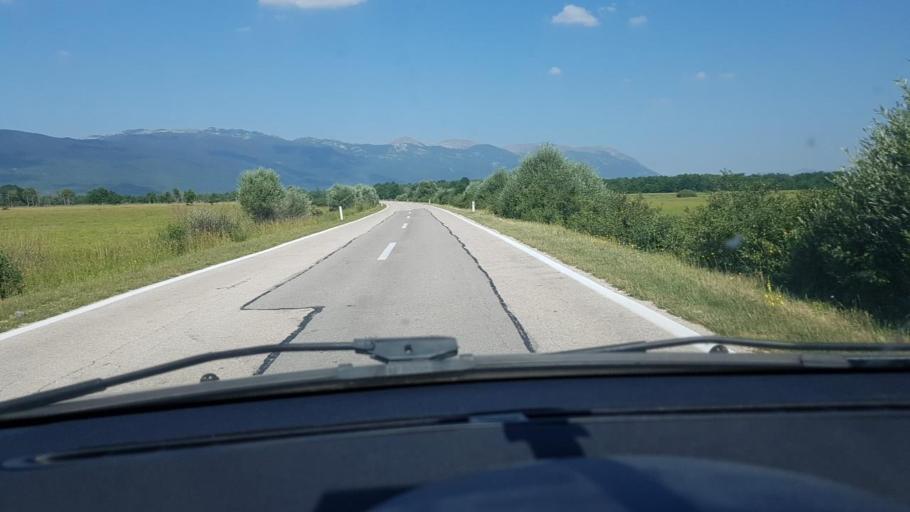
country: BA
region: Federation of Bosnia and Herzegovina
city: Glamoc
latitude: 43.9828
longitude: 16.6956
